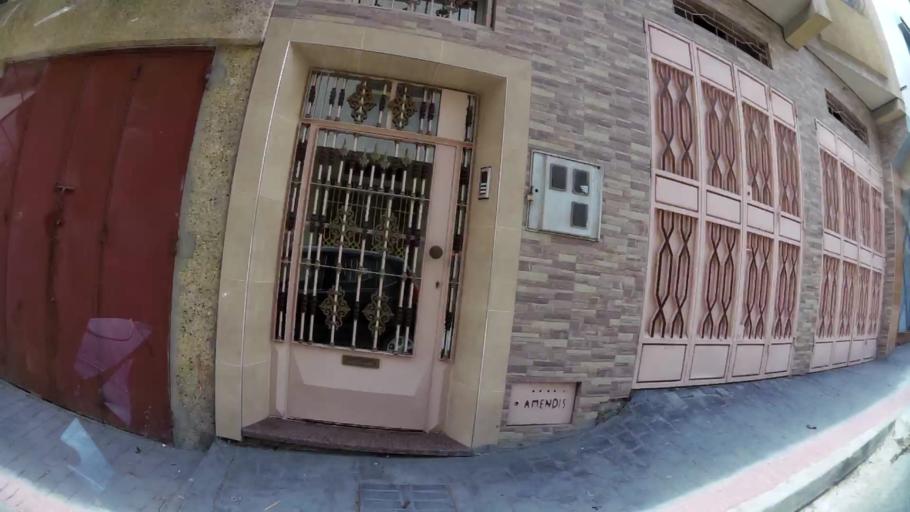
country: MA
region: Tanger-Tetouan
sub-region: Tanger-Assilah
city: Tangier
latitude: 35.7550
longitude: -5.8152
